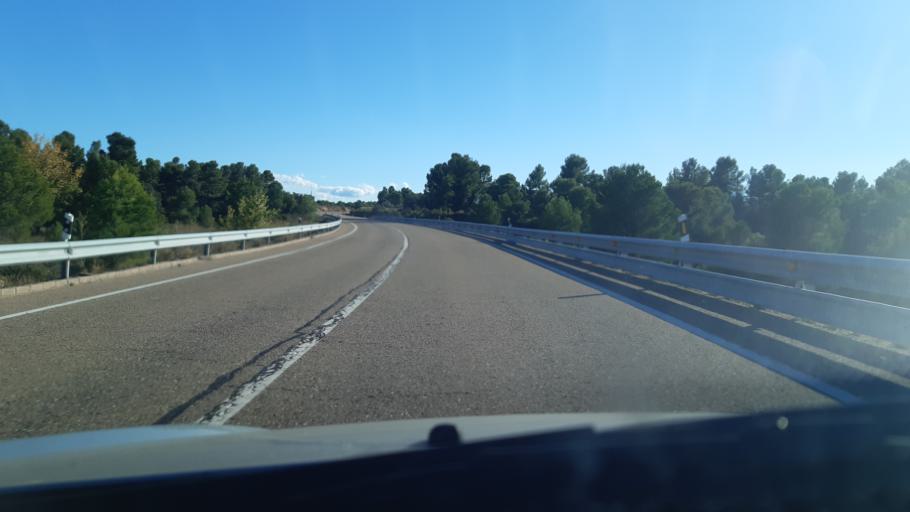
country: ES
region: Aragon
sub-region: Provincia de Teruel
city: Fornoles
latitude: 40.9225
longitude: -0.0192
